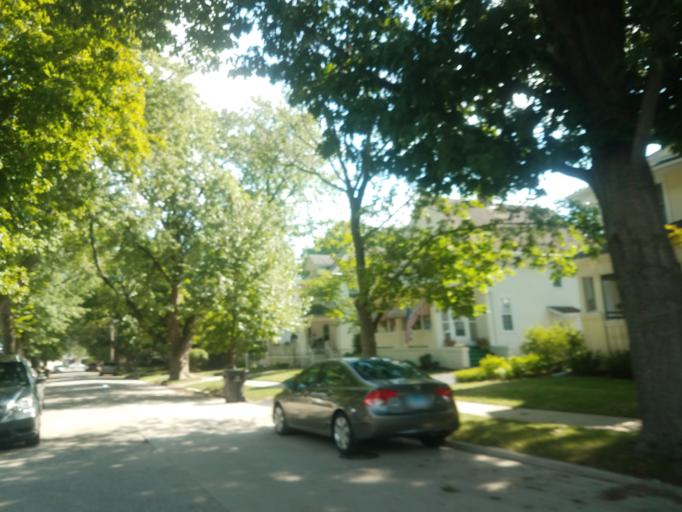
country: US
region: Illinois
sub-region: McLean County
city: Bloomington
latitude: 40.4753
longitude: -88.9690
